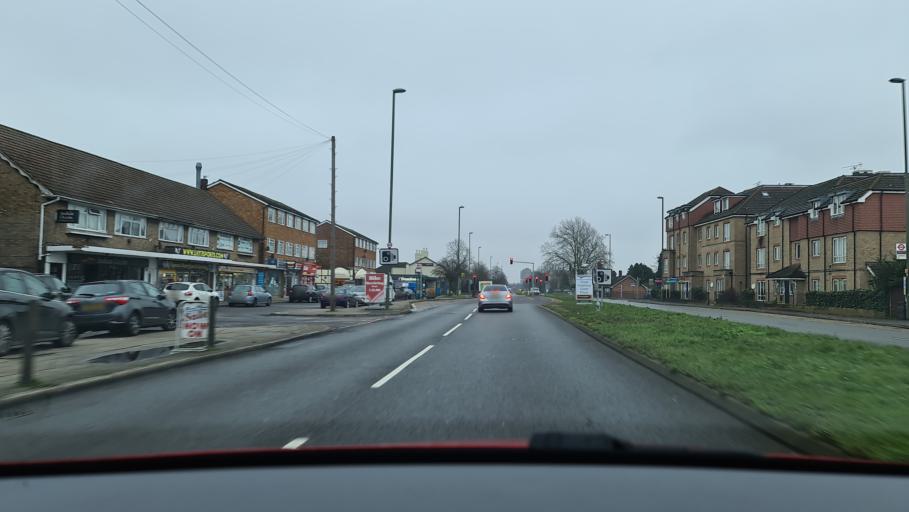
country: GB
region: England
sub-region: Surrey
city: Shepperton
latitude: 51.4223
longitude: -0.4426
